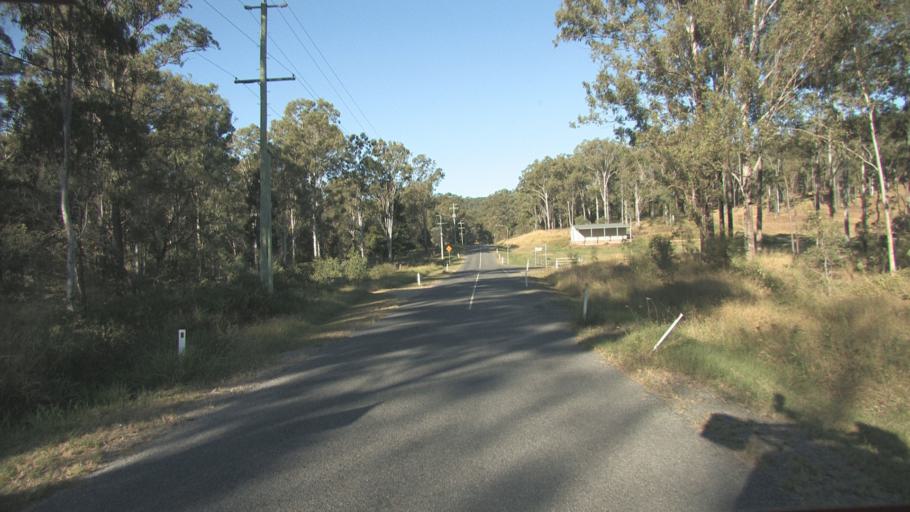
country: AU
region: Queensland
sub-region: Logan
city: Windaroo
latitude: -27.7716
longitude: 153.1453
